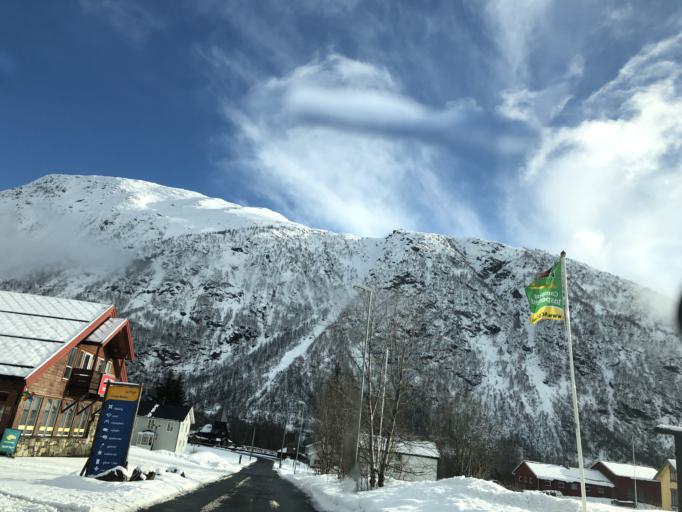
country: NO
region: Hordaland
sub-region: Odda
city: Odda
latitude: 59.8323
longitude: 6.8187
